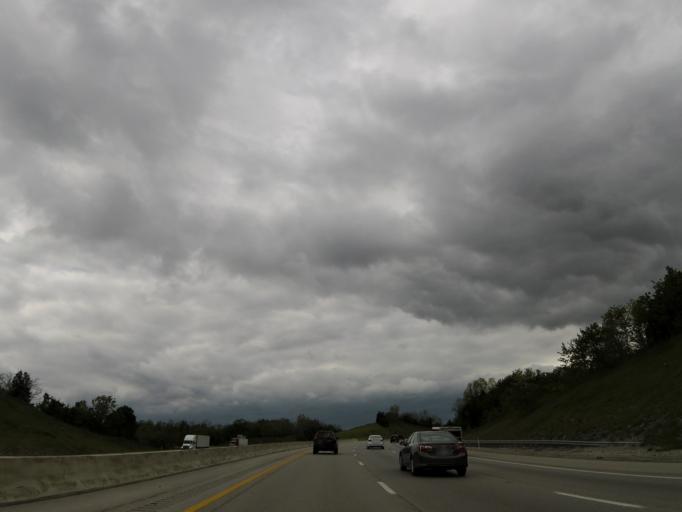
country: US
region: Kentucky
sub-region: Scott County
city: Georgetown
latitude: 38.4099
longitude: -84.5795
